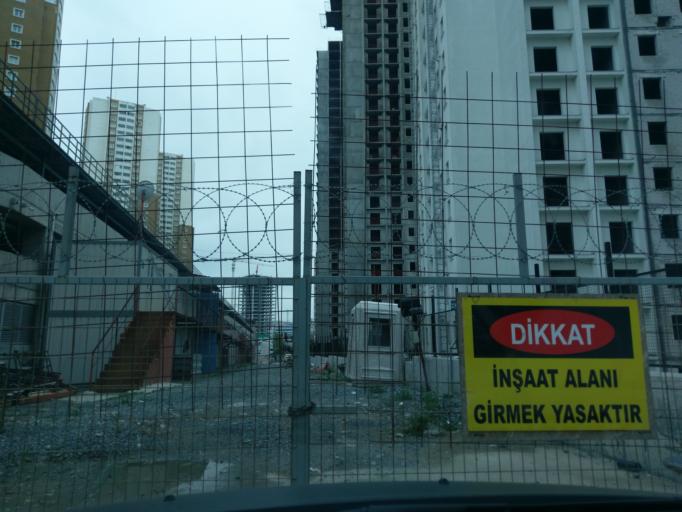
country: TR
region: Istanbul
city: Esenyurt
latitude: 41.0167
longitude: 28.6751
